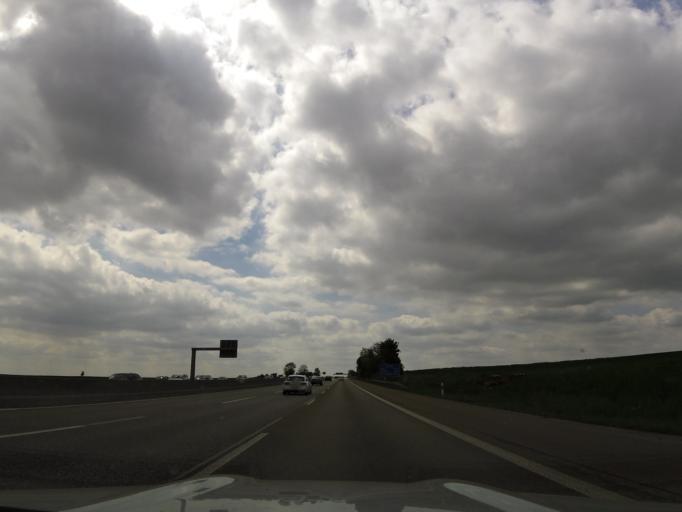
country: DE
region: Hesse
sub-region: Regierungsbezirk Darmstadt
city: Butzbach
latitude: 50.4311
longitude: 8.6962
